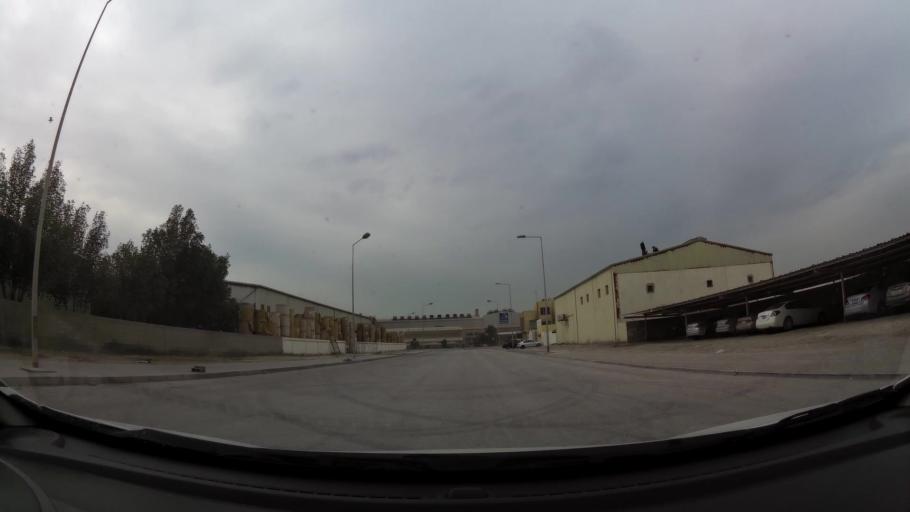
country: BH
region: Northern
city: Sitrah
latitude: 26.1832
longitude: 50.6167
